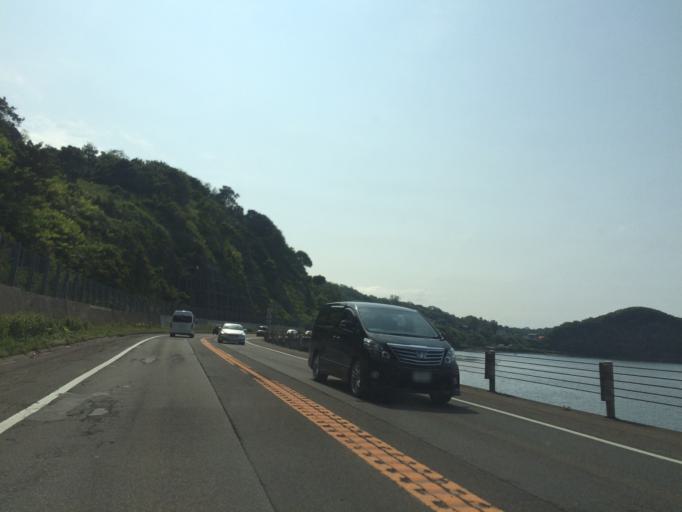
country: JP
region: Hokkaido
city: Yoichi
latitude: 43.2053
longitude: 140.8777
